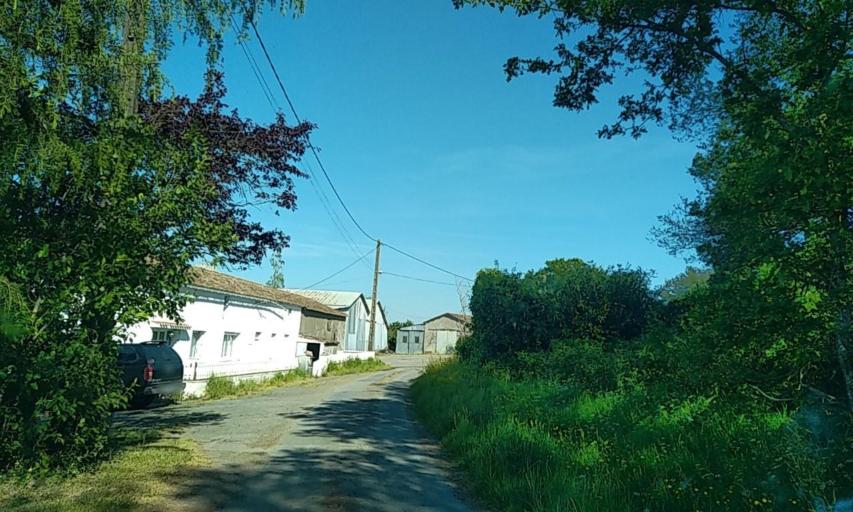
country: FR
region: Poitou-Charentes
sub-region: Departement des Deux-Sevres
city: Boisme
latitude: 46.8066
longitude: -0.4151
